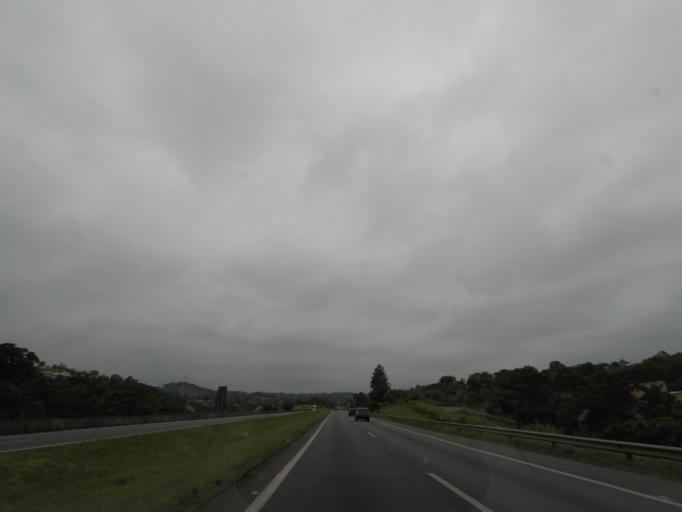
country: BR
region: Sao Paulo
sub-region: Jarinu
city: Jarinu
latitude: -23.0298
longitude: -46.7426
